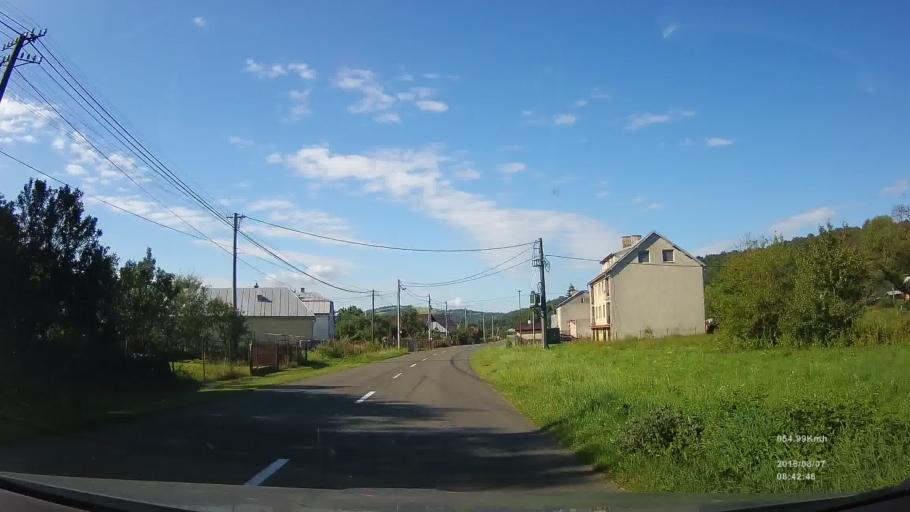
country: SK
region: Presovsky
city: Stropkov
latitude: 49.2820
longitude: 21.7566
